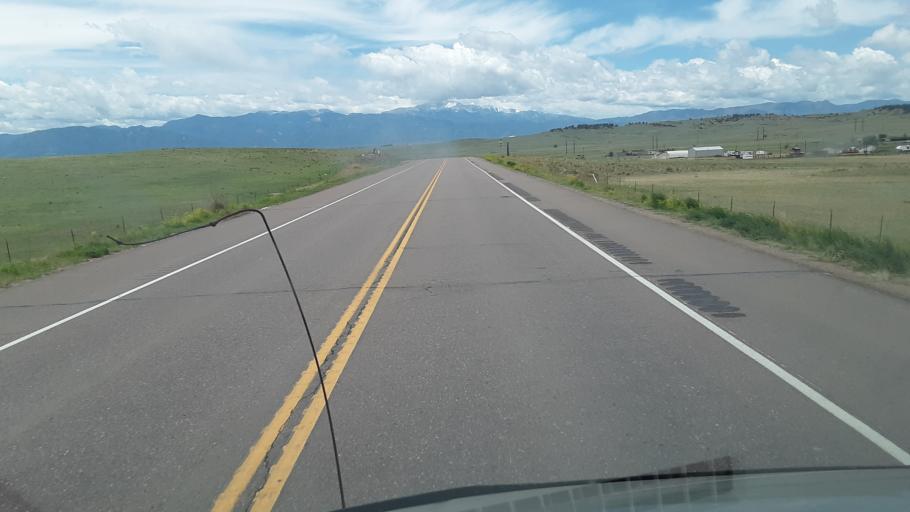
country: US
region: Colorado
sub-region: El Paso County
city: Cimarron Hills
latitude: 38.8388
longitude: -104.6078
